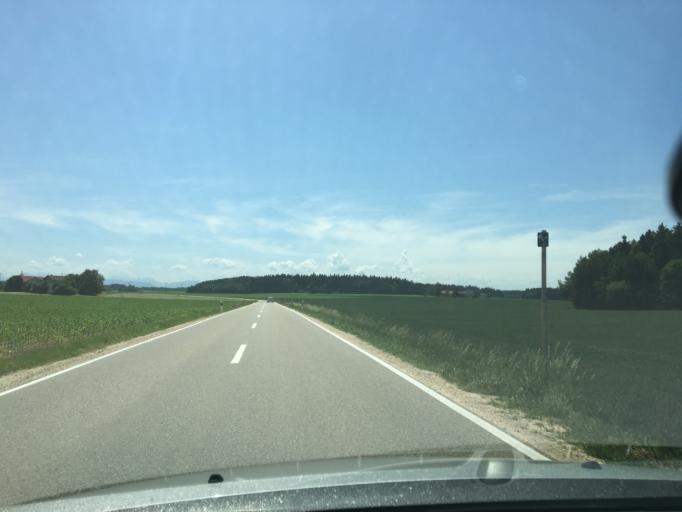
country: DE
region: Bavaria
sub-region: Upper Bavaria
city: Halsbach
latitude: 48.1071
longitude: 12.6831
